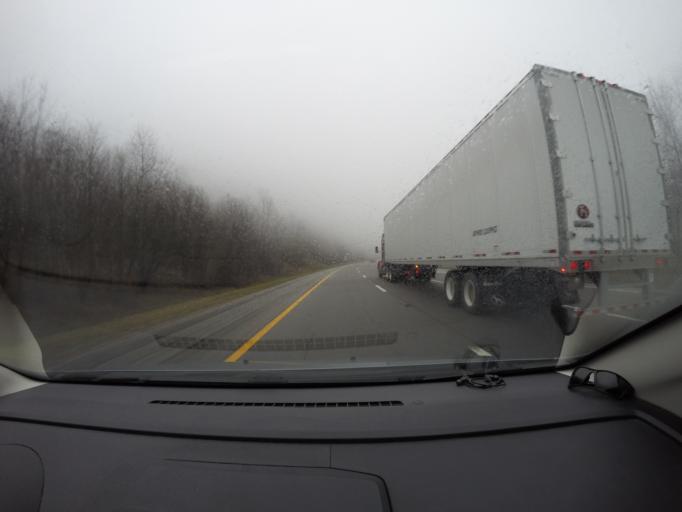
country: US
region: Tennessee
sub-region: Marion County
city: Monteagle
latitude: 35.2047
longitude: -85.8153
